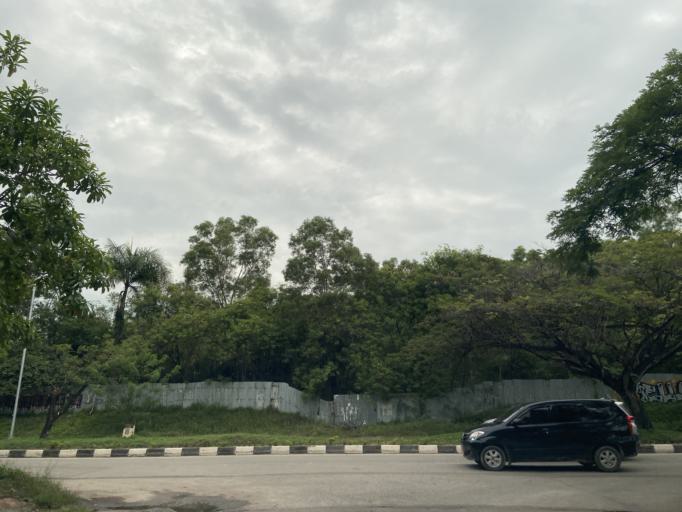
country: SG
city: Singapore
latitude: 1.1287
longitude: 104.0496
